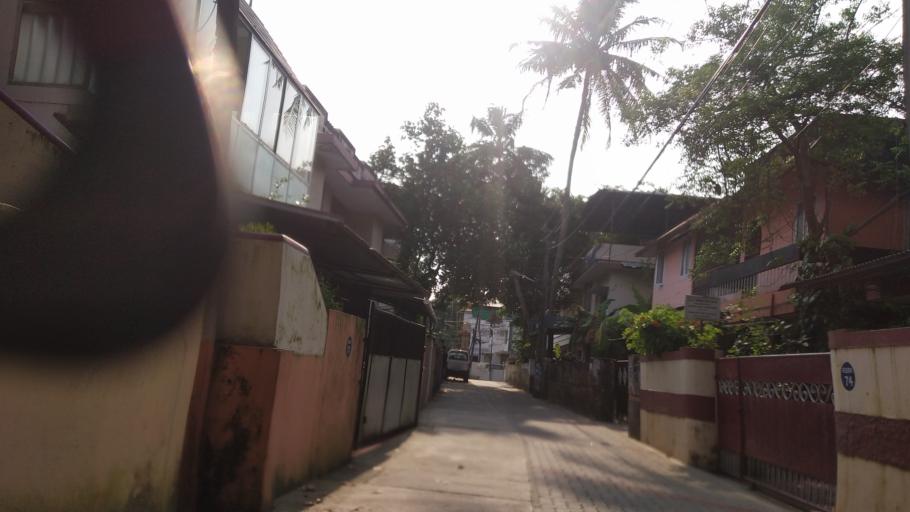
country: IN
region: Kerala
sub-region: Ernakulam
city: Elur
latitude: 10.0001
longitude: 76.2957
